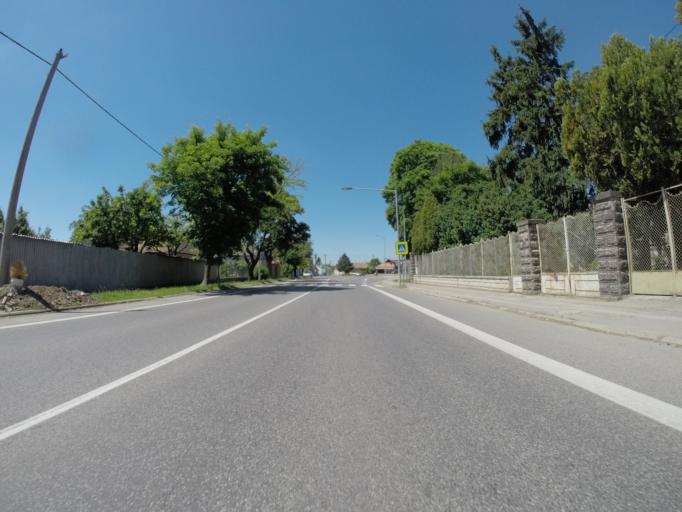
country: SK
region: Trnavsky
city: Hlohovec
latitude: 48.4380
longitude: 17.8055
